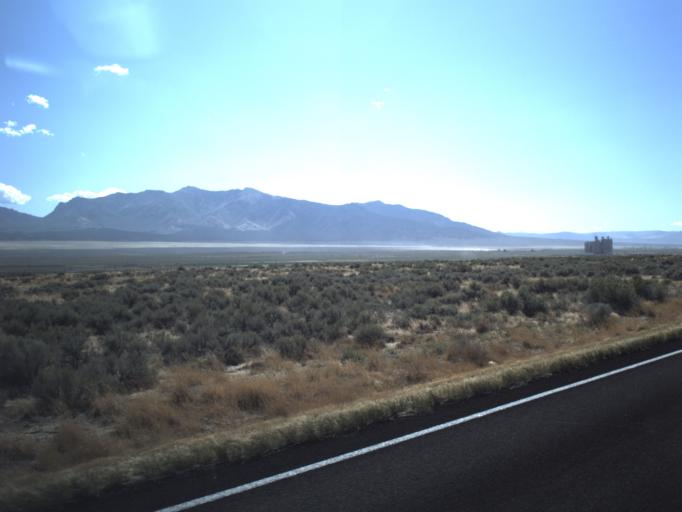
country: US
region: Utah
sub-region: Beaver County
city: Milford
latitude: 38.4129
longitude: -113.0099
